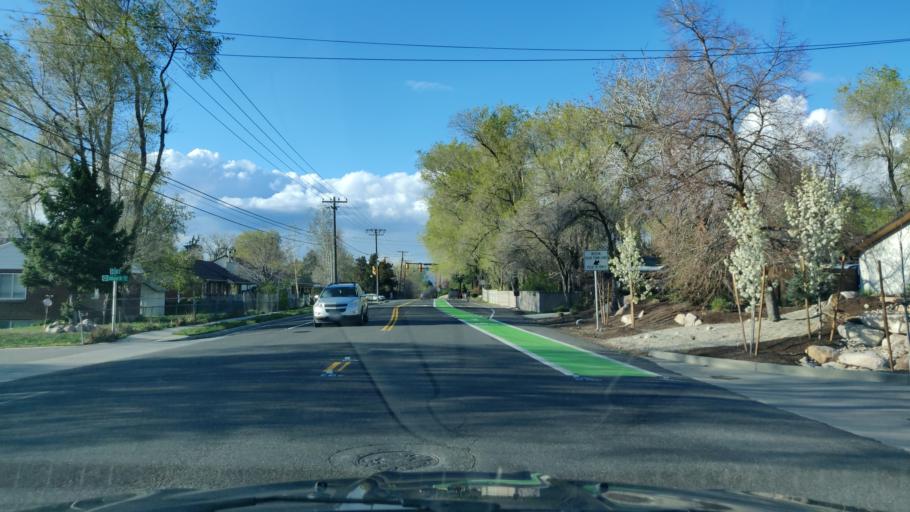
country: US
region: Utah
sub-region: Salt Lake County
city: Cottonwood Heights
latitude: 40.6372
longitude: -111.8247
